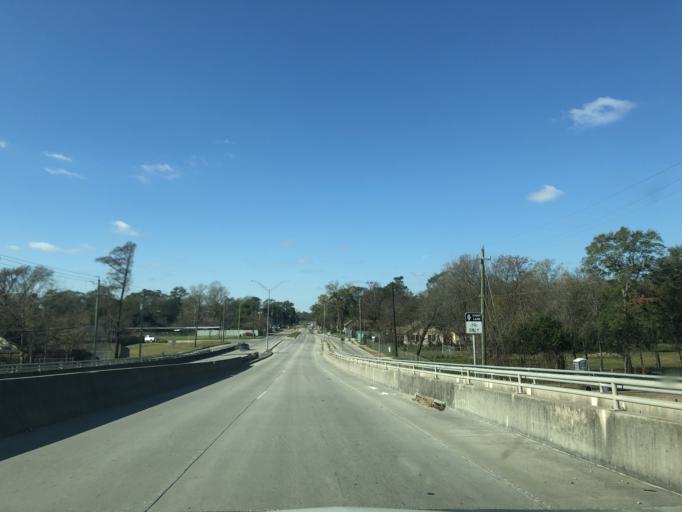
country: US
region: Texas
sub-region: Harris County
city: Jacinto City
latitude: 29.8314
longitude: -95.2899
